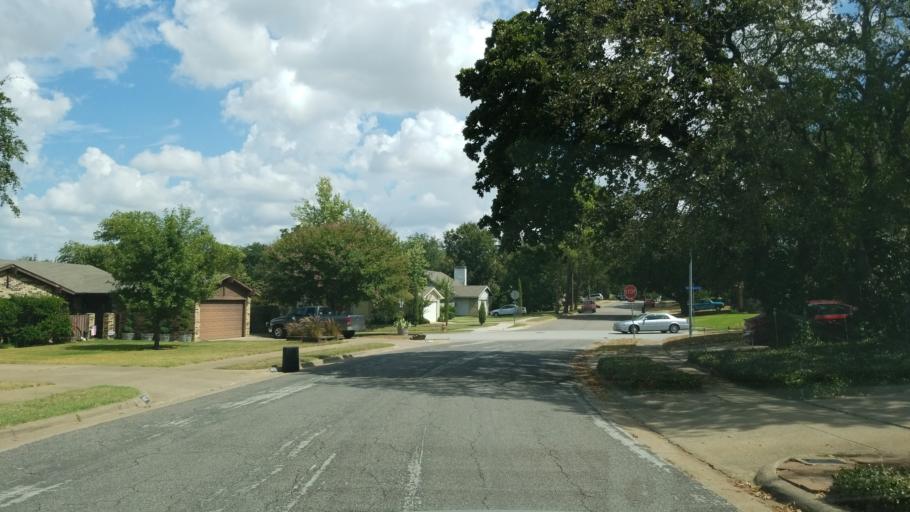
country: US
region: Texas
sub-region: Tarrant County
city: Euless
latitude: 32.8575
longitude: -97.0887
